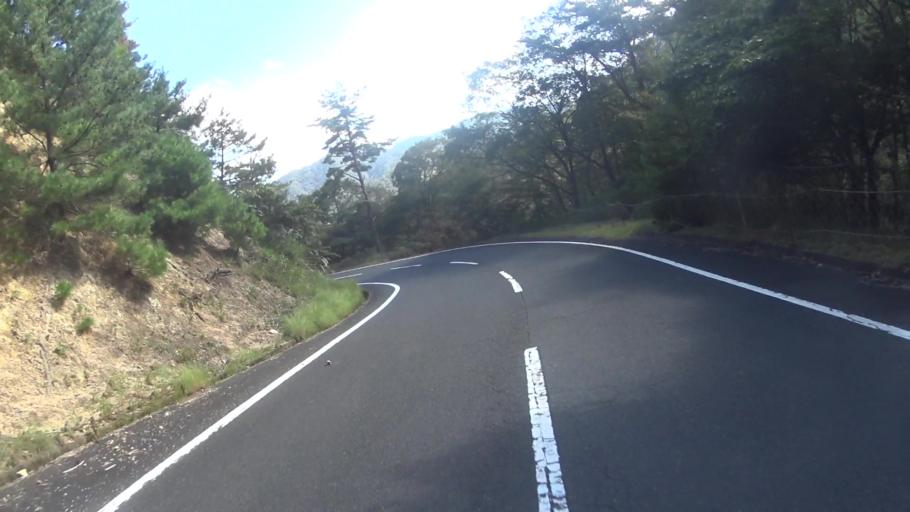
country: JP
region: Hyogo
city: Toyooka
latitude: 35.5365
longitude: 134.9207
